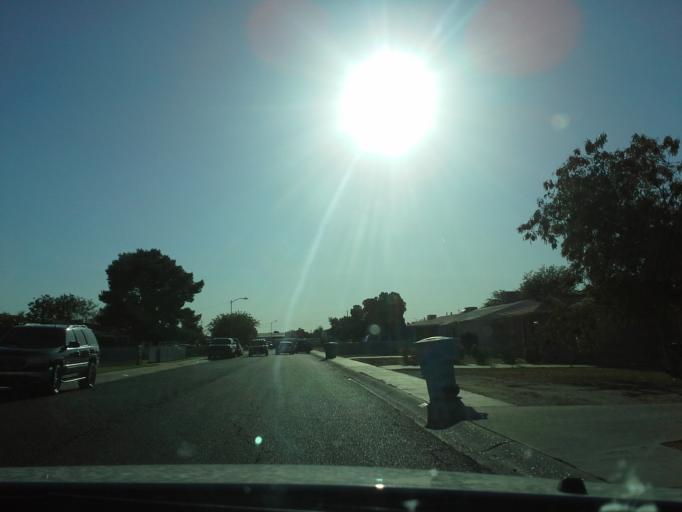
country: US
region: Arizona
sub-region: Maricopa County
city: Phoenix
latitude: 33.4317
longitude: -112.0968
